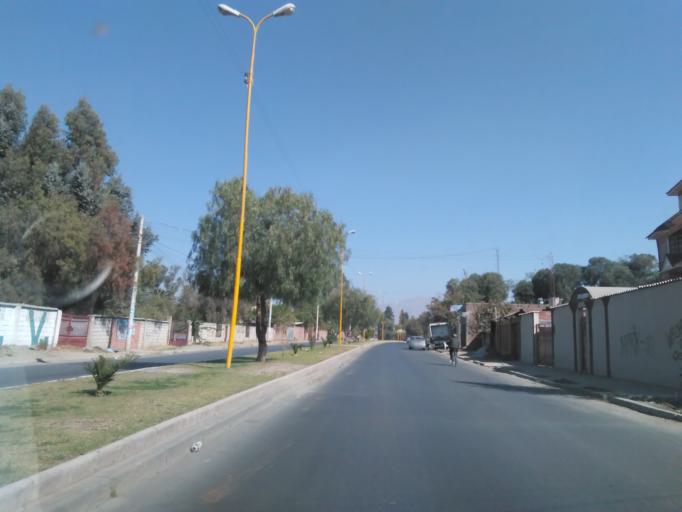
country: BO
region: Cochabamba
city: Cochabamba
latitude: -17.3936
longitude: -66.2665
